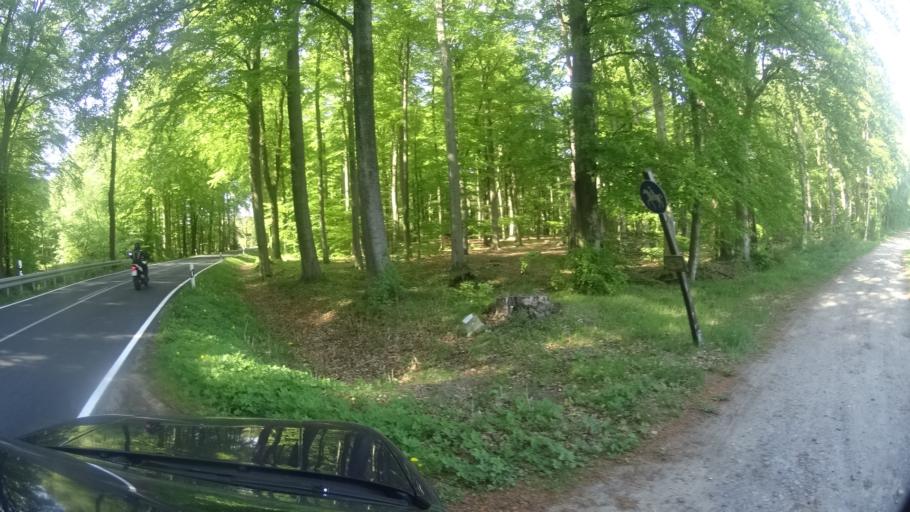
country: DE
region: Mecklenburg-Vorpommern
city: Gelbensande
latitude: 54.2503
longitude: 12.3116
